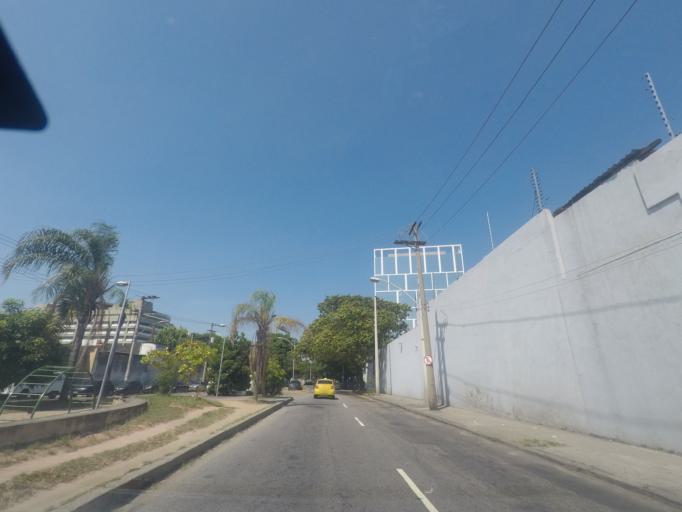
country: BR
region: Rio de Janeiro
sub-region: Rio De Janeiro
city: Rio de Janeiro
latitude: -22.8963
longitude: -43.2160
